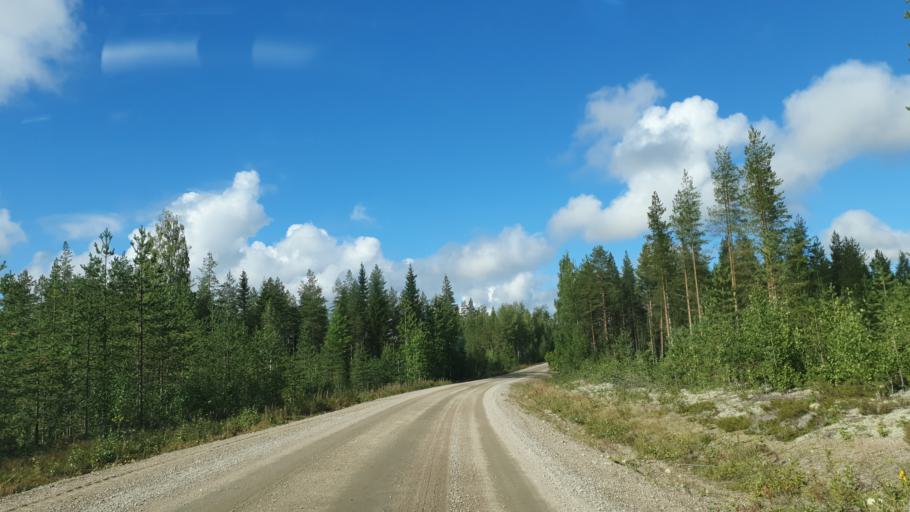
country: FI
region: Kainuu
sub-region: Kehys-Kainuu
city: Kuhmo
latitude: 63.9839
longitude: 29.2333
